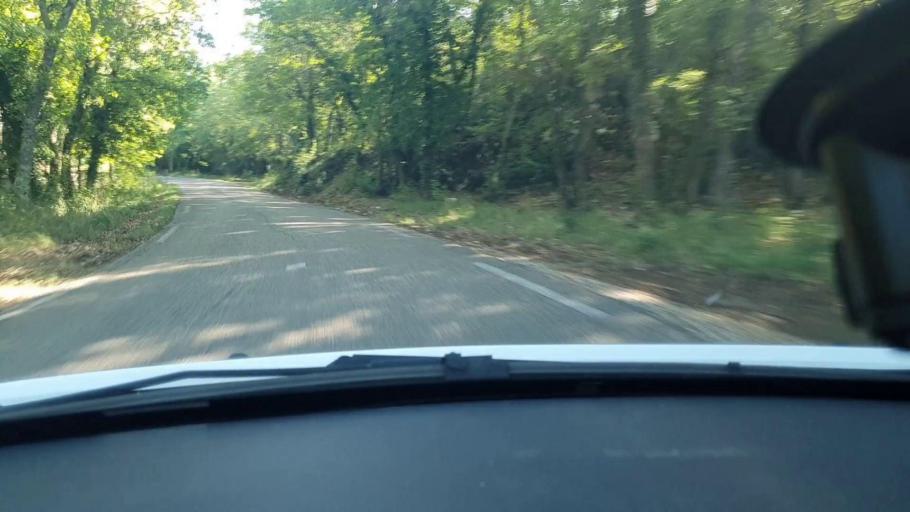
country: FR
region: Languedoc-Roussillon
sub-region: Departement du Gard
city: Goudargues
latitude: 44.2287
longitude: 4.3991
